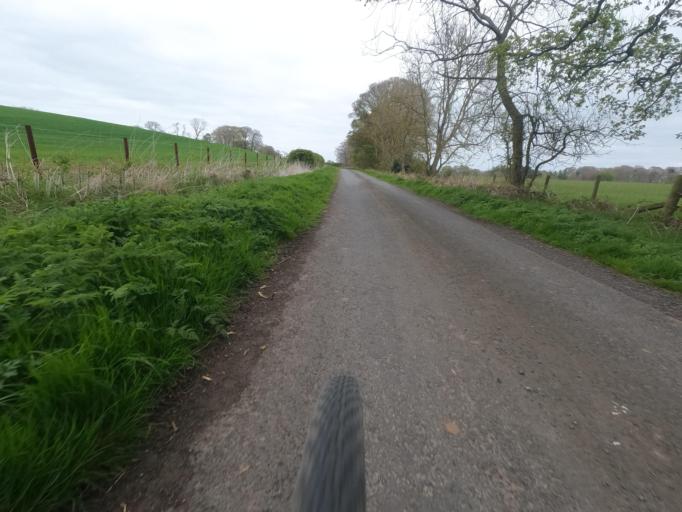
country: GB
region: England
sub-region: Northumberland
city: Meldon
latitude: 55.0663
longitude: -1.8352
